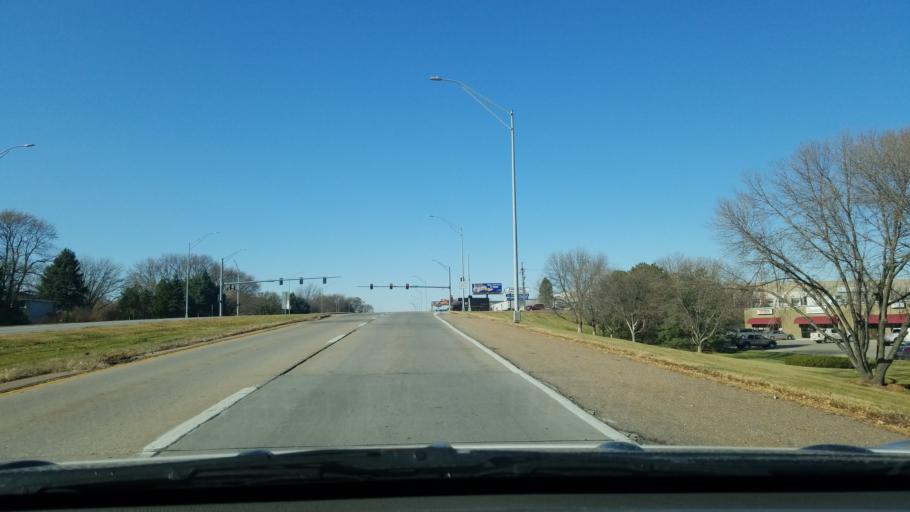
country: US
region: Nebraska
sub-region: Douglas County
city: Ralston
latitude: 41.2126
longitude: -96.0701
